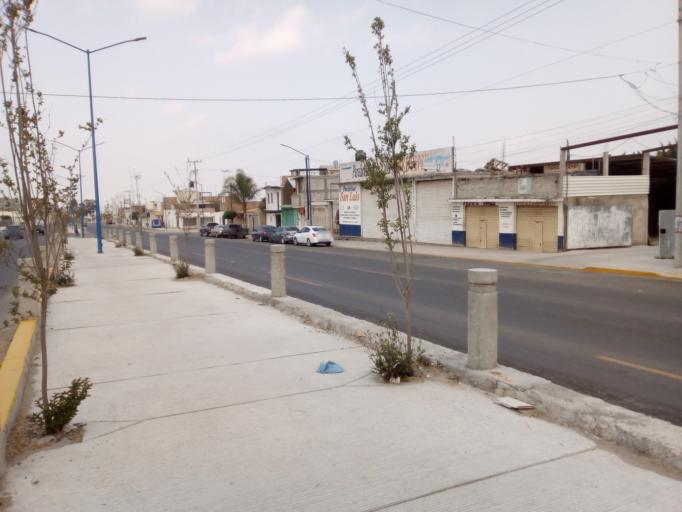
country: MX
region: Guerrero
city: San Luis de la Paz
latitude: 21.2882
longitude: -100.5170
